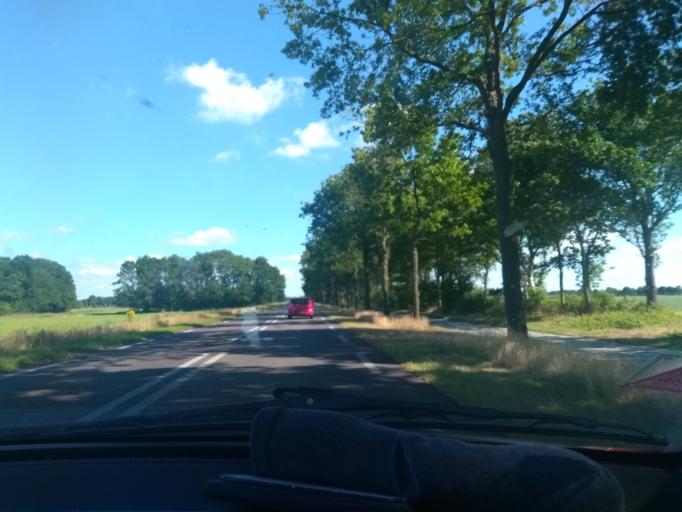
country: NL
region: Drenthe
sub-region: Gemeente Tynaarlo
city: Vries
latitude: 53.1167
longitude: 6.5118
